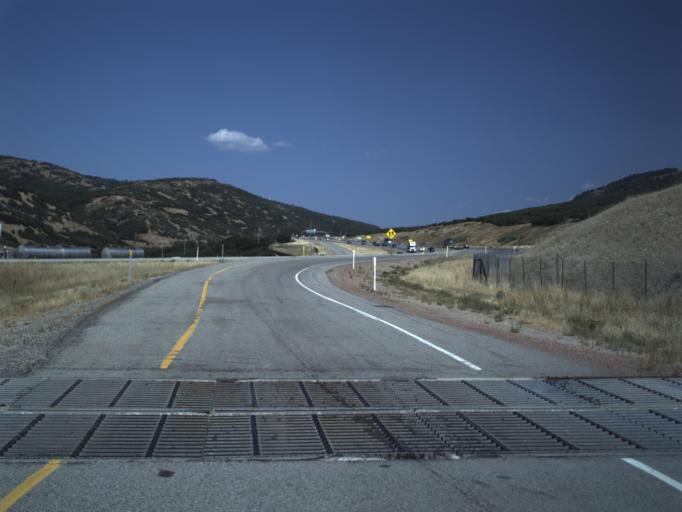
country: US
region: Utah
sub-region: Summit County
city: Summit Park
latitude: 40.7384
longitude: -111.6725
